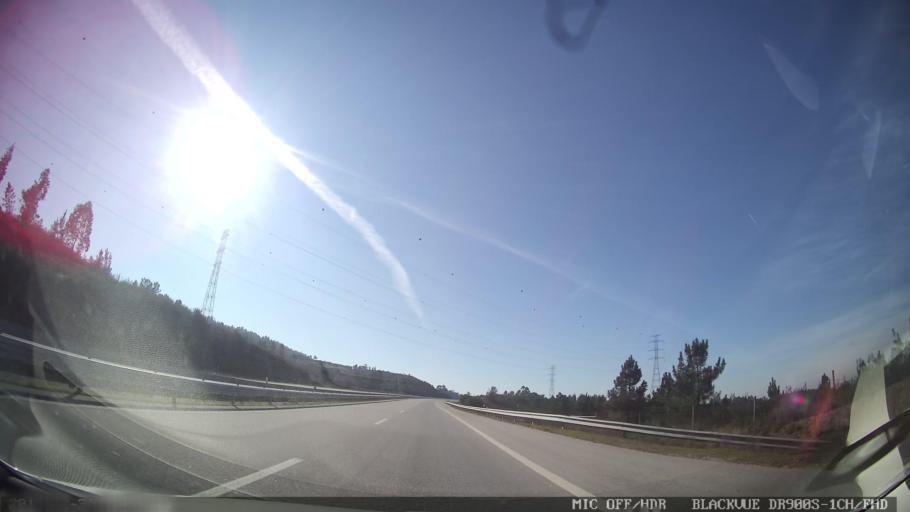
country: PT
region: Castelo Branco
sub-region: Castelo Branco
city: Castelo Branco
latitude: 39.7755
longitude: -7.5863
